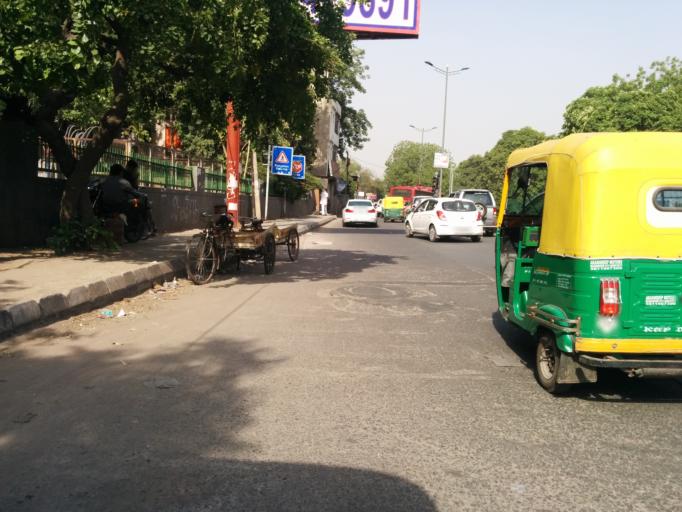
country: IN
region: NCT
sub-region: New Delhi
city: New Delhi
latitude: 28.5292
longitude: 77.2141
